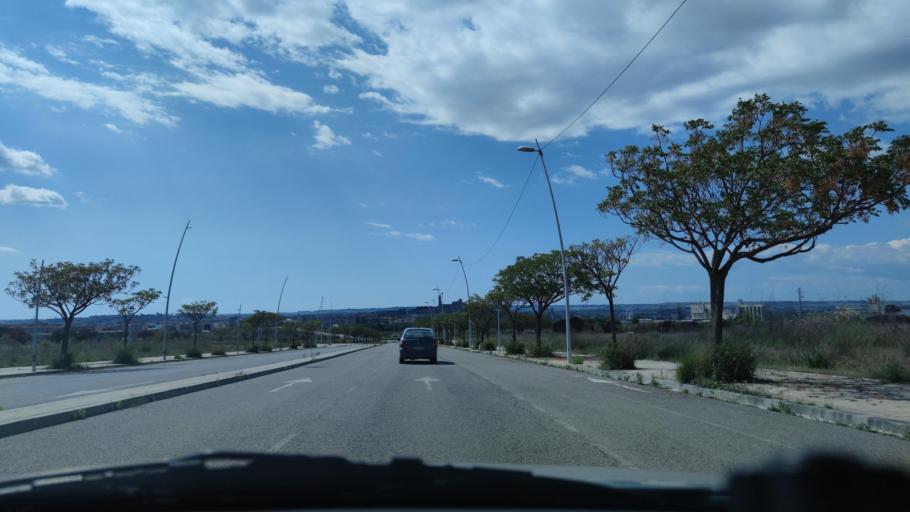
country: ES
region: Catalonia
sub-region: Provincia de Lleida
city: Lleida
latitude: 41.6056
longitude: 0.6588
